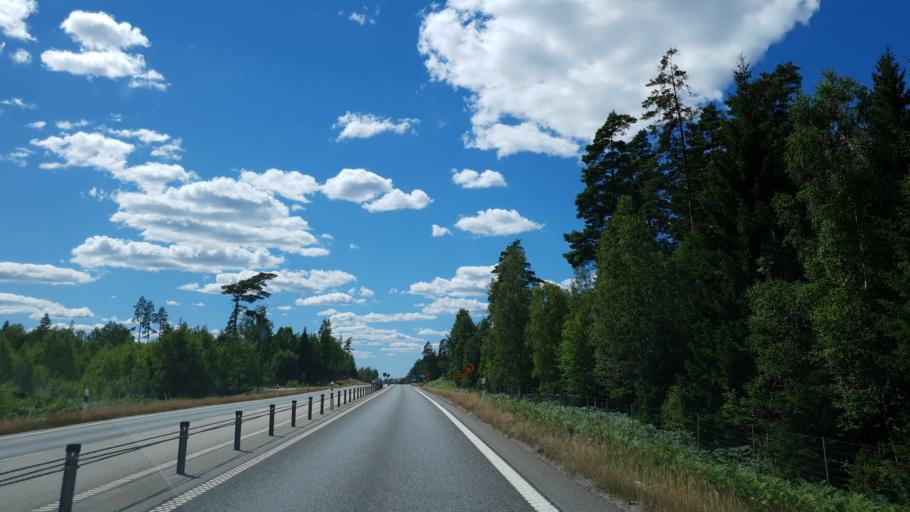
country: SE
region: Kronoberg
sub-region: Vaxjo Kommun
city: Vaexjoe
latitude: 56.8846
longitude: 14.8649
